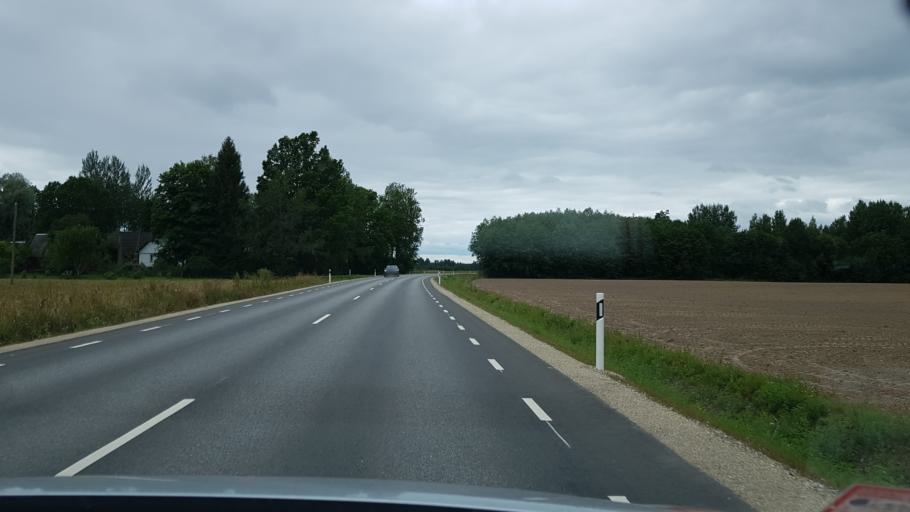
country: EE
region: Polvamaa
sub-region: Polva linn
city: Polva
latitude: 58.0762
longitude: 27.2518
